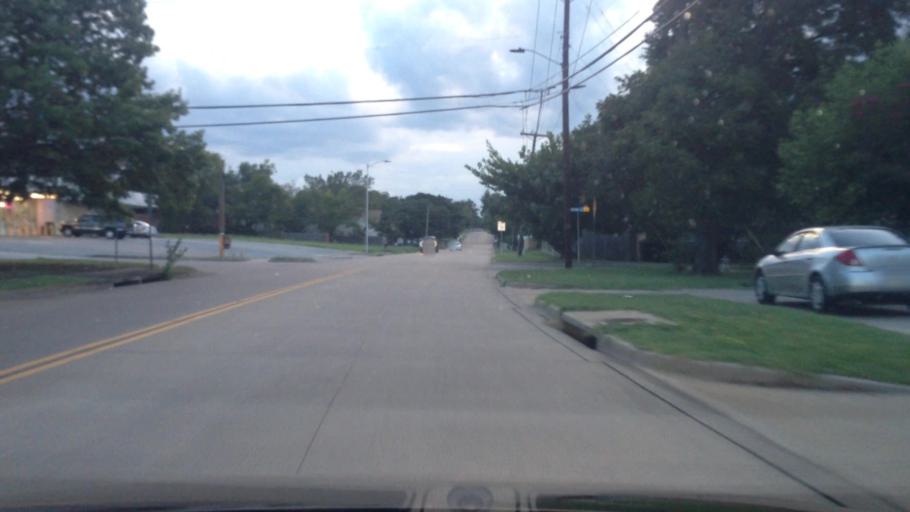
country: US
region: Texas
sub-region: Tarrant County
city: Arlington
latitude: 32.7429
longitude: -97.1325
